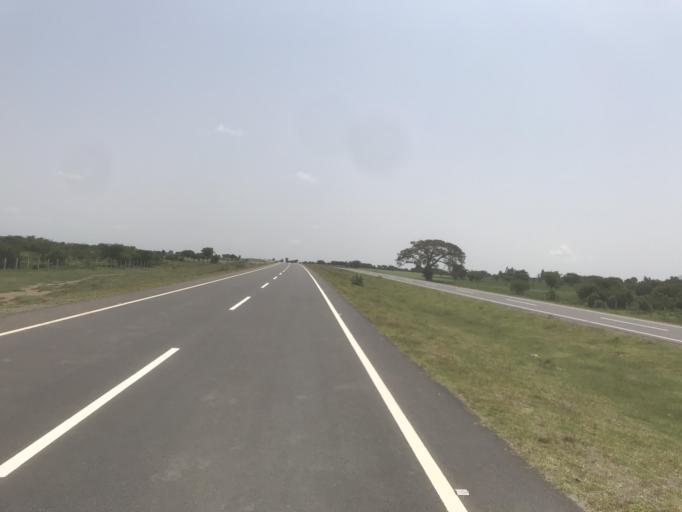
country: ET
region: Oromiya
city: Ziway
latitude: 8.2584
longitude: 38.8973
